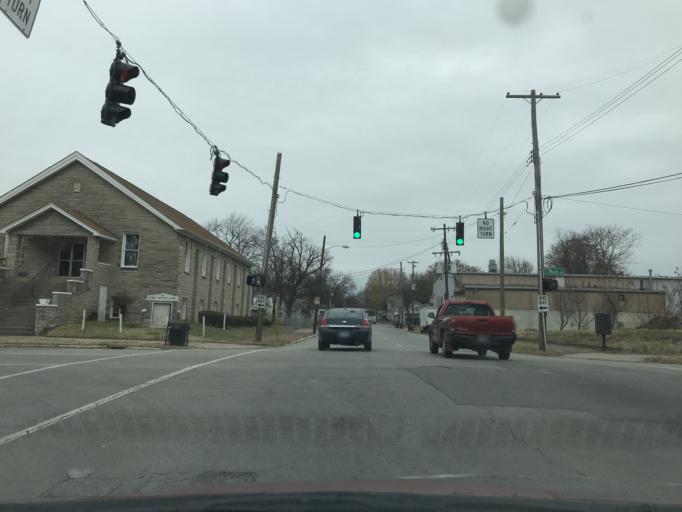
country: US
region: Kentucky
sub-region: Jefferson County
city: Louisville
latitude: 38.2597
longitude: -85.7847
